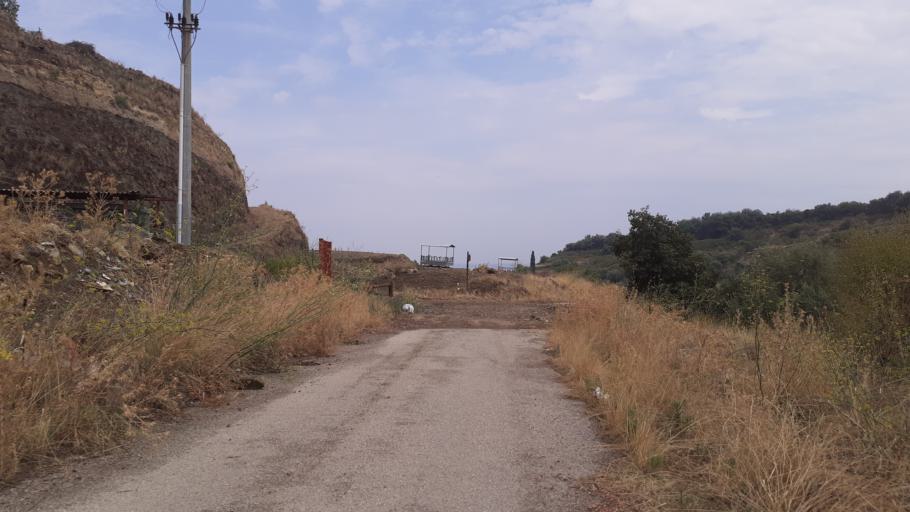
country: IT
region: Sicily
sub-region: Catania
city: Militello in Val di Catania
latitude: 37.2813
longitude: 14.8166
